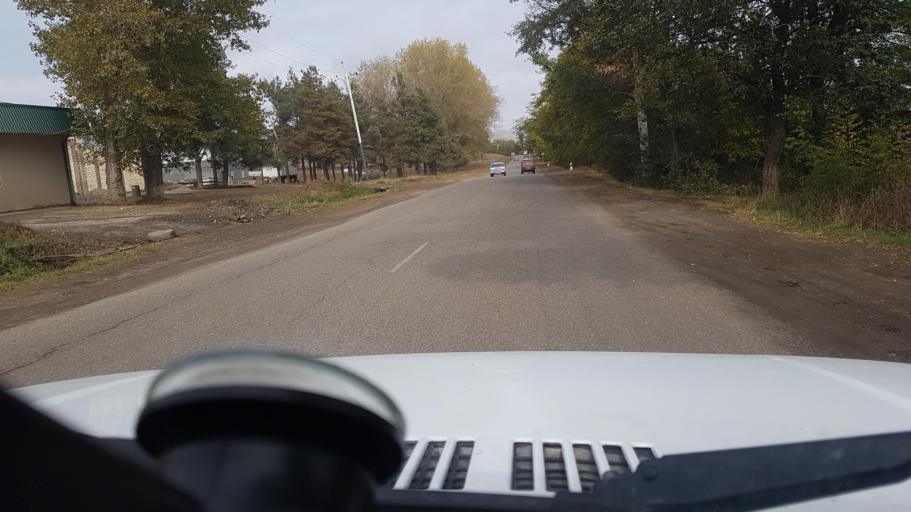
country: AZ
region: Gadabay Rayon
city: Ariqdam
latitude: 40.6426
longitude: 45.8129
